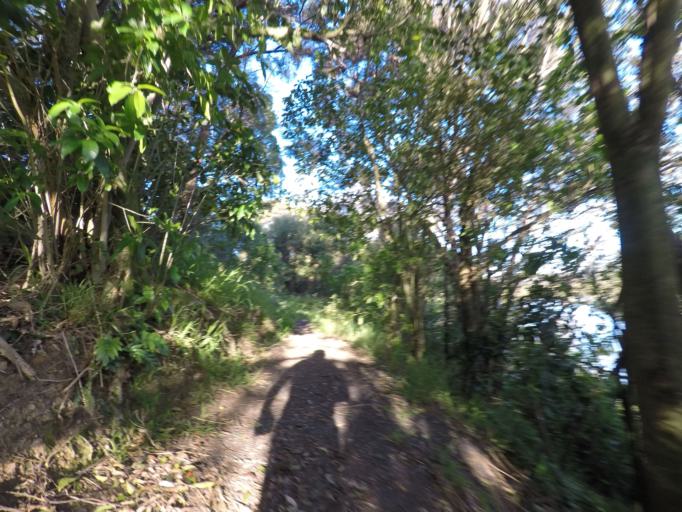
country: NZ
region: Auckland
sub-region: Auckland
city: Rosebank
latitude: -36.8430
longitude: 174.6367
